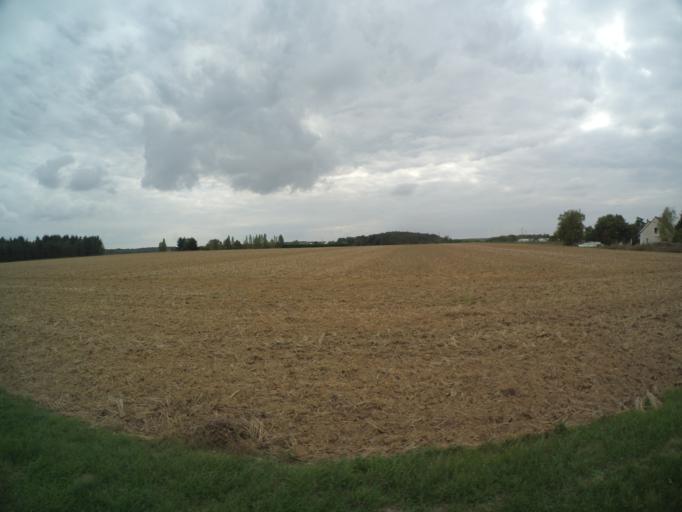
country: FR
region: Centre
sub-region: Departement d'Indre-et-Loire
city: Poce-sur-Cisse
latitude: 47.5026
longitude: 0.9777
